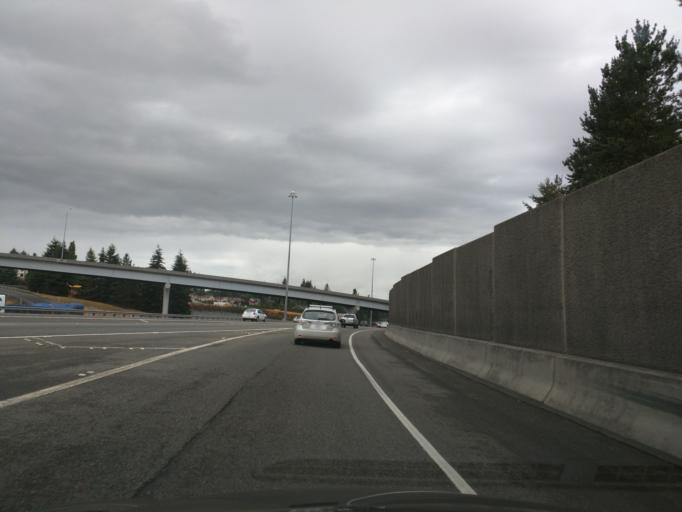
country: US
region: Washington
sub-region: Snohomish County
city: Mill Creek
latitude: 47.9190
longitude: -122.2059
